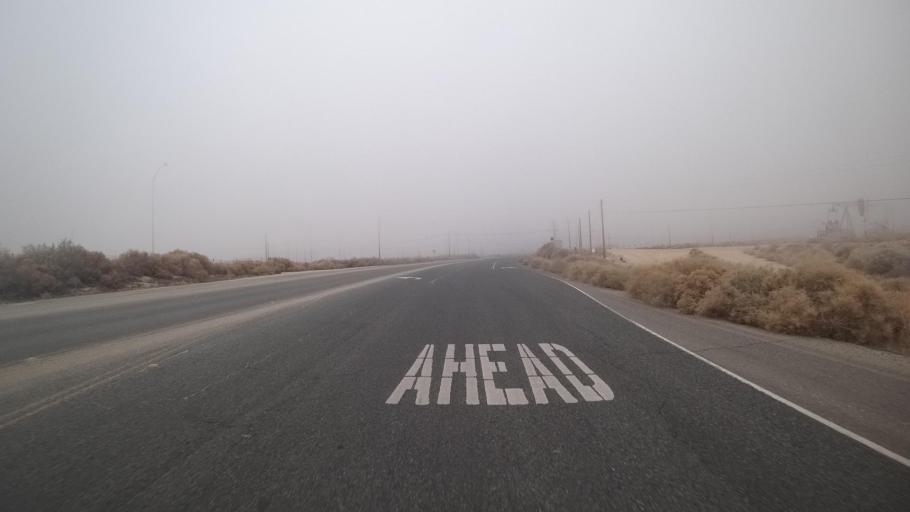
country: US
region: California
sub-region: Kern County
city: Ford City
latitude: 35.2765
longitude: -119.4678
